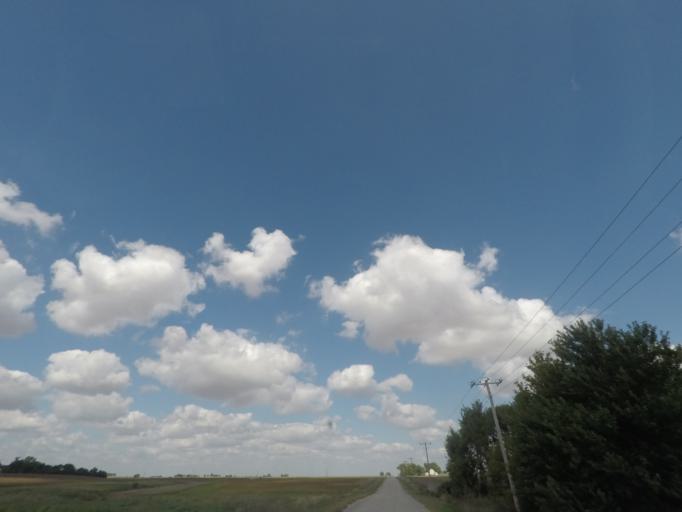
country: US
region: Iowa
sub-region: Story County
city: Nevada
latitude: 42.0741
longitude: -93.3864
